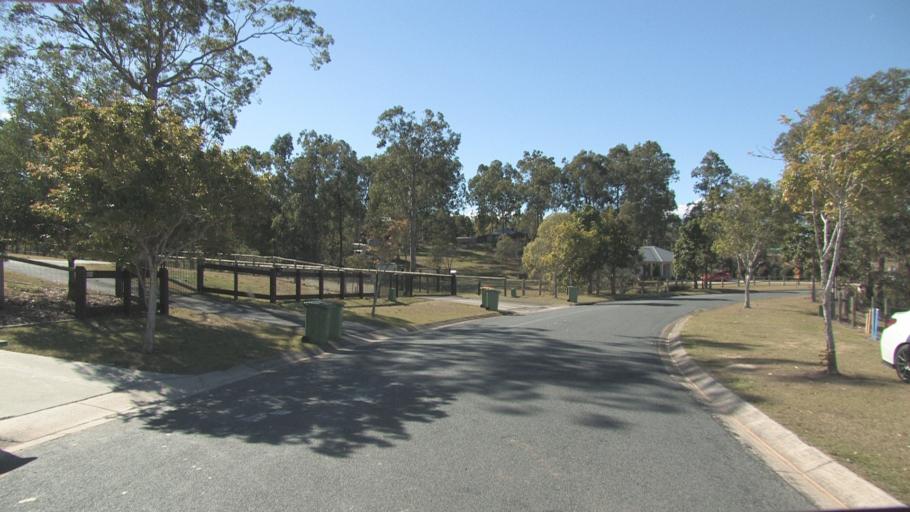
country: AU
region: Queensland
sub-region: Ipswich
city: Springfield Lakes
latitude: -27.7241
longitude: 152.9171
